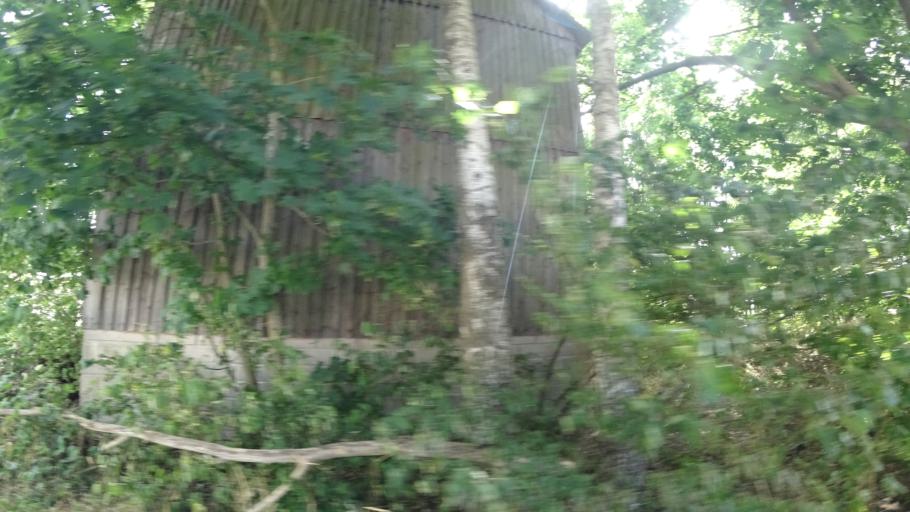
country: SE
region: Skane
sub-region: Kristianstads Kommun
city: Fjalkinge
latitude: 55.9872
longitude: 14.2694
